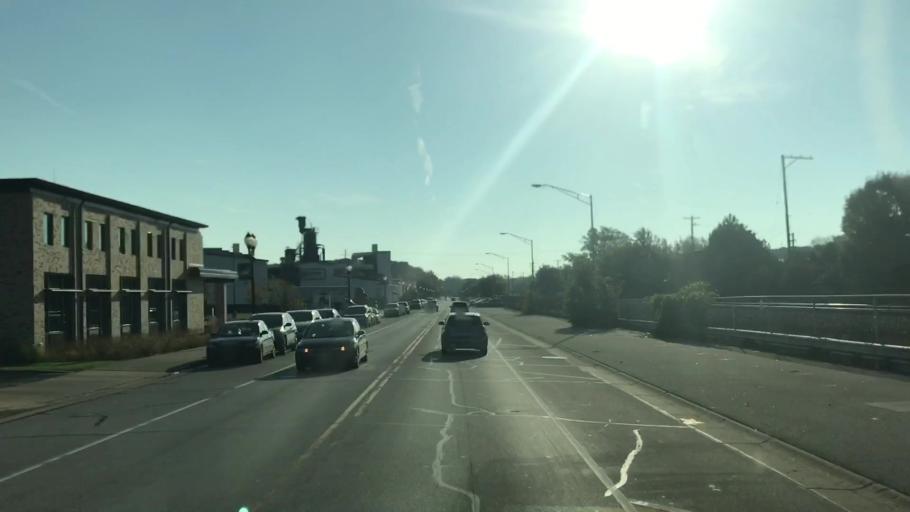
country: US
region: Wisconsin
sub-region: Milwaukee County
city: Wauwatosa
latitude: 43.0454
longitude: -87.9950
